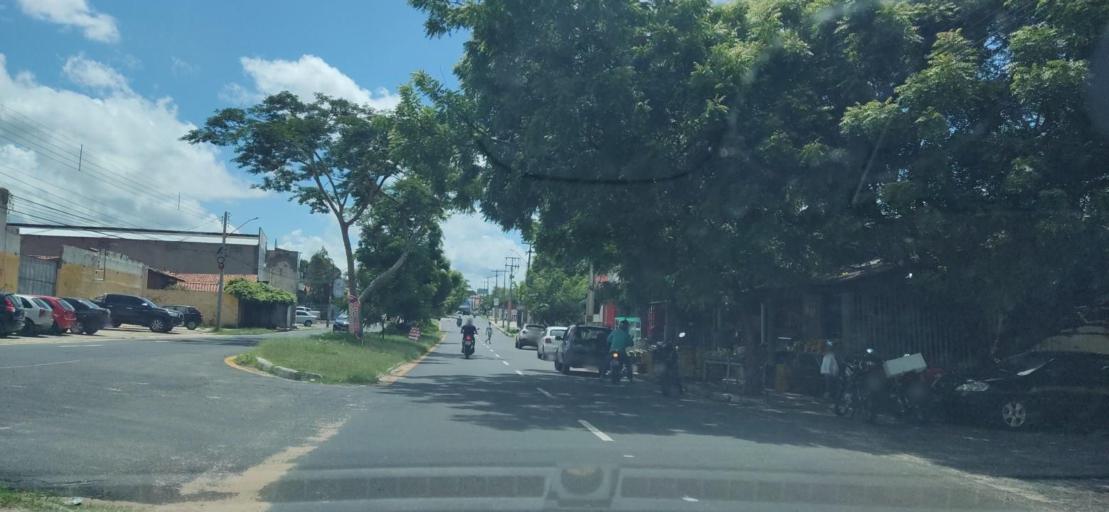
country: BR
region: Piaui
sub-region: Teresina
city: Teresina
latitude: -5.0648
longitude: -42.7642
